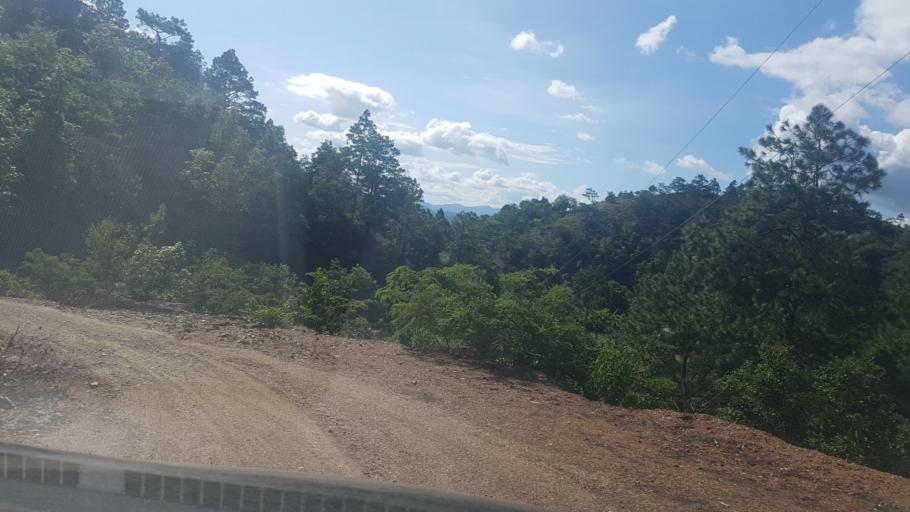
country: HN
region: Choluteca
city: Duyure
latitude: 13.6479
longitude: -86.6546
